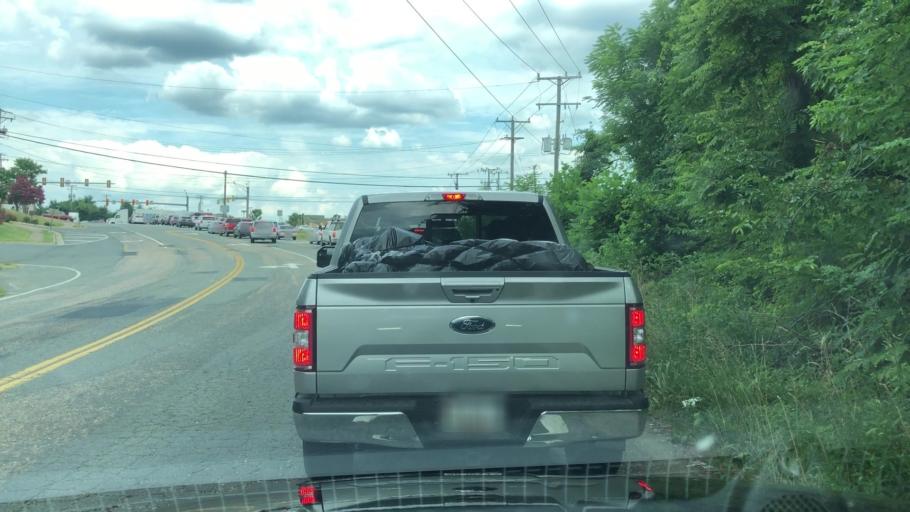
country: US
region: Virginia
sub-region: Stafford County
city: Falmouth
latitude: 38.3420
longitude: -77.4978
